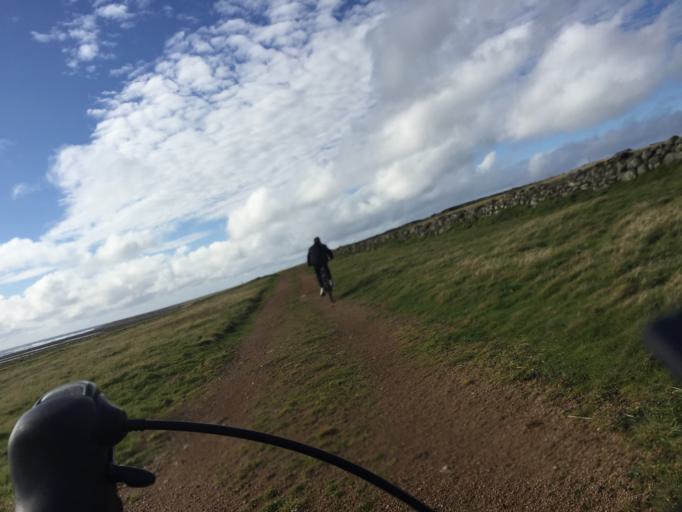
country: IE
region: Ulster
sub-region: County Donegal
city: Derrybeg
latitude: 55.2625
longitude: -8.2332
